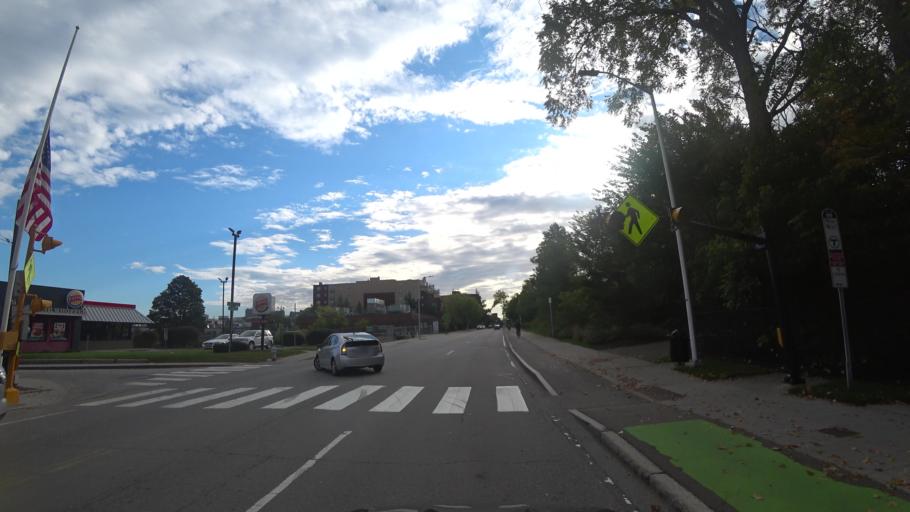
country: US
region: Massachusetts
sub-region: Middlesex County
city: Arlington
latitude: 42.3902
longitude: -71.1513
